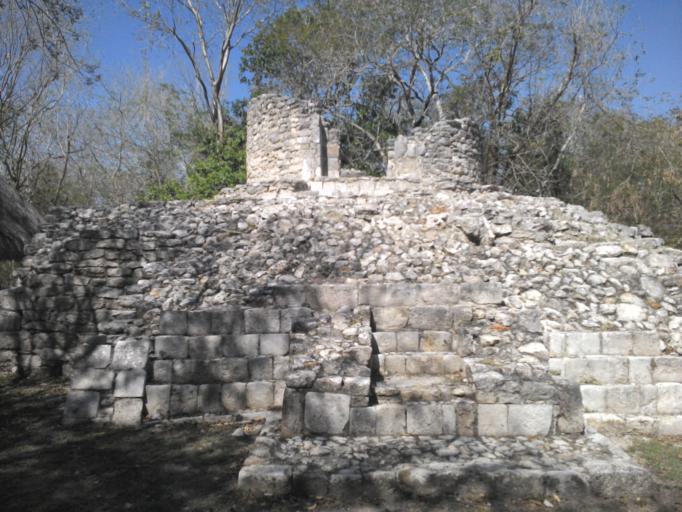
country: MX
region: Yucatan
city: Tekoh
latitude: 20.6289
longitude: -89.4590
